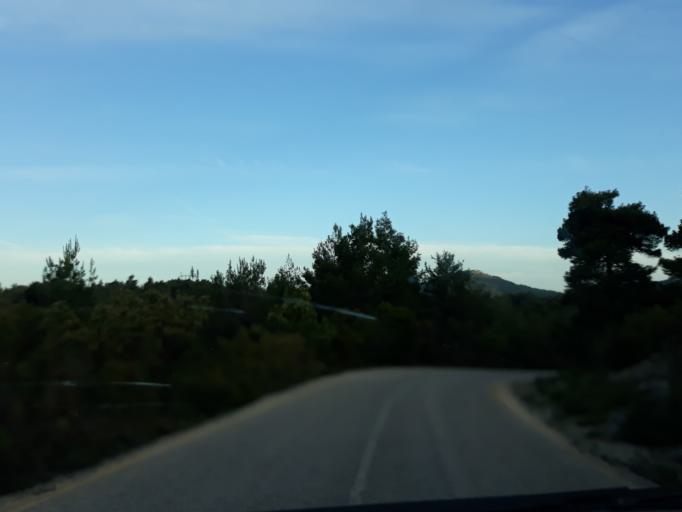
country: GR
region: Attica
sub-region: Nomarchia Anatolikis Attikis
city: Afidnes
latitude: 38.2059
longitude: 23.7888
